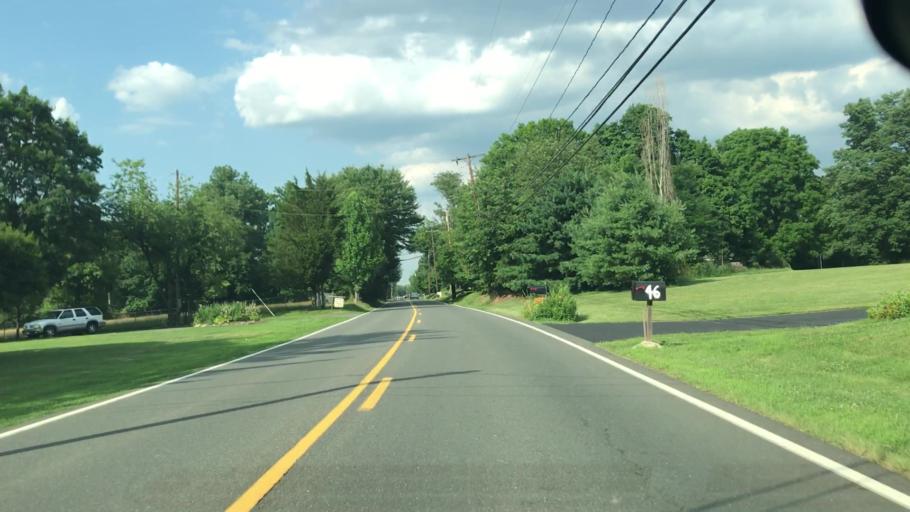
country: US
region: New Jersey
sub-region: Hunterdon County
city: Flemington
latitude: 40.4483
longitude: -74.8469
